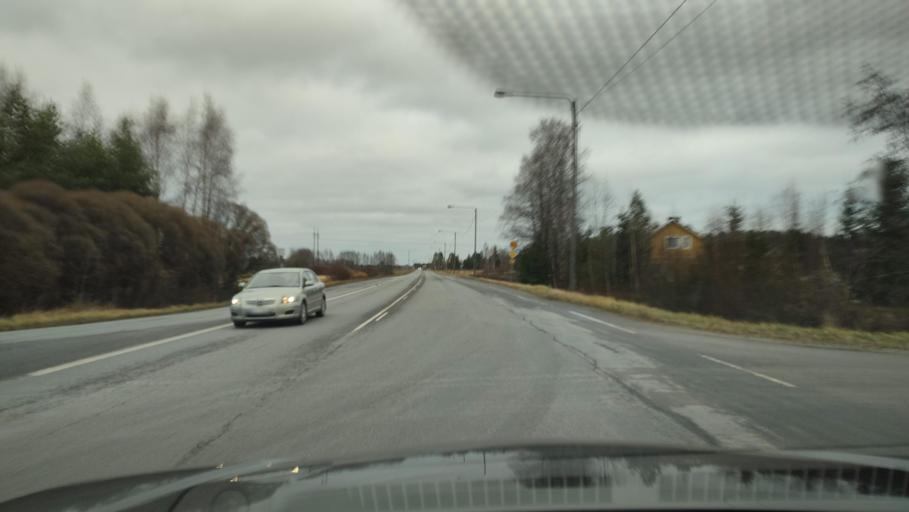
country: FI
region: Southern Ostrobothnia
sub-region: Seinaejoki
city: Kurikka
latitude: 62.6827
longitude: 22.4814
